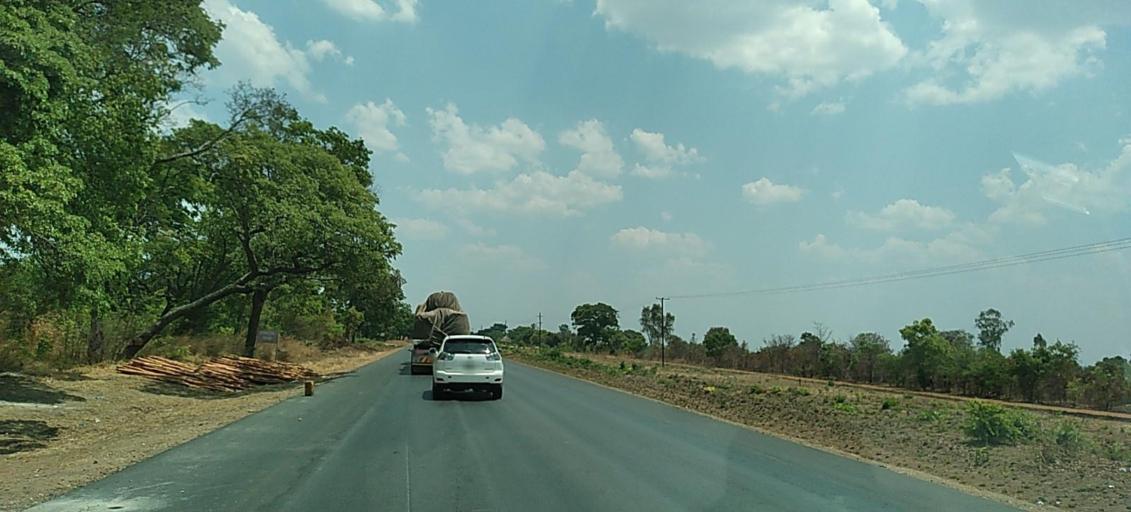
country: ZM
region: Central
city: Kabwe
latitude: -14.2685
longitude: 28.5548
